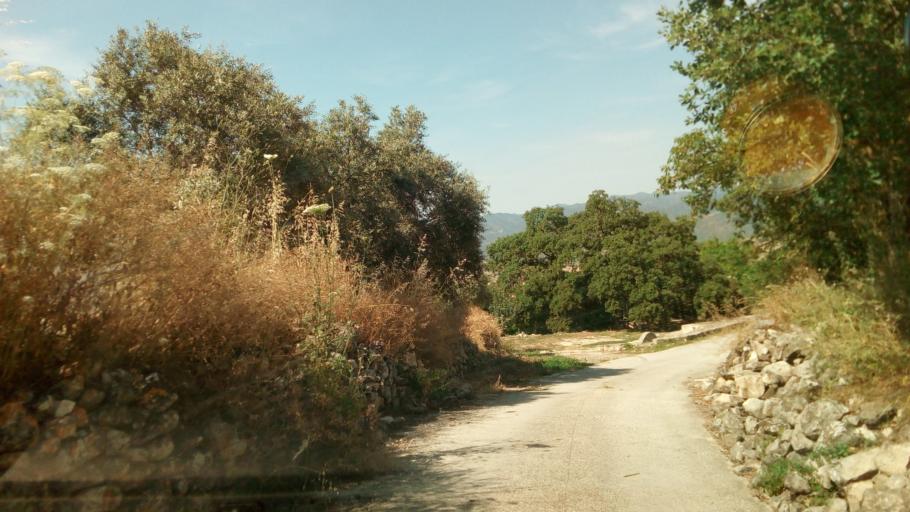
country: CY
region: Pafos
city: Tala
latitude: 34.9285
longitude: 32.5288
